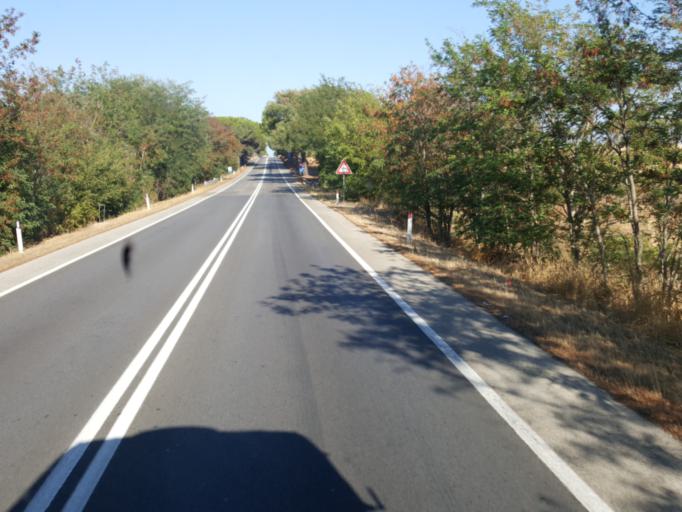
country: IT
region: Tuscany
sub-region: Provincia di Grosseto
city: Capalbio
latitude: 42.4144
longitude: 11.4493
